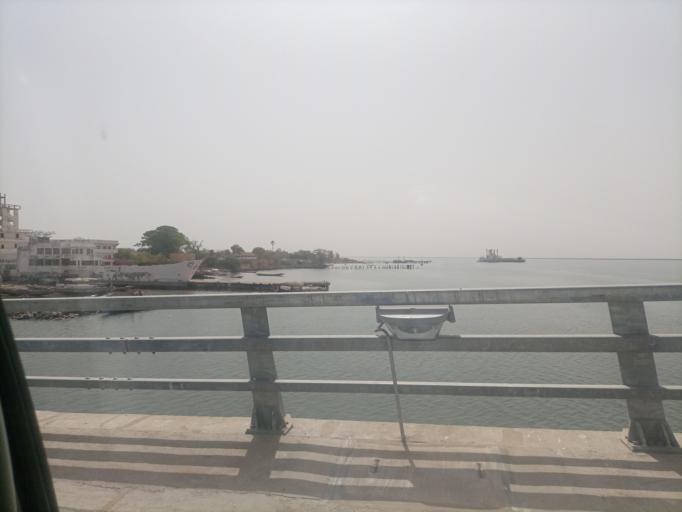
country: SN
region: Fatick
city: Foundiougne
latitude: 14.1312
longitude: -16.4669
